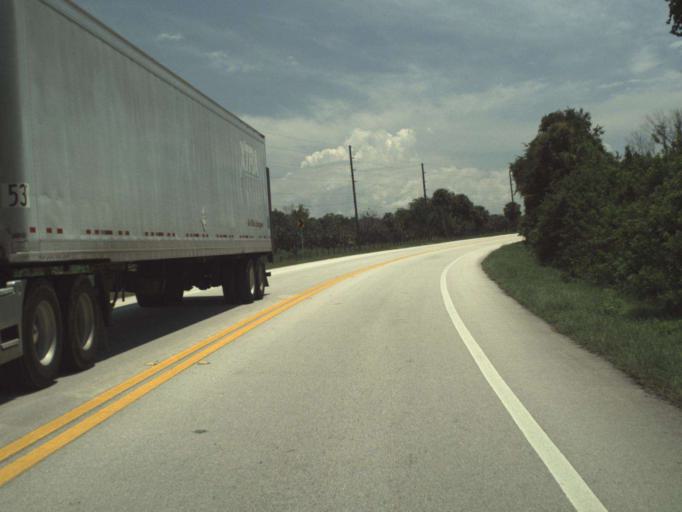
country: US
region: Florida
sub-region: Okeechobee County
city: Taylor Creek
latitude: 27.1005
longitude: -80.6577
